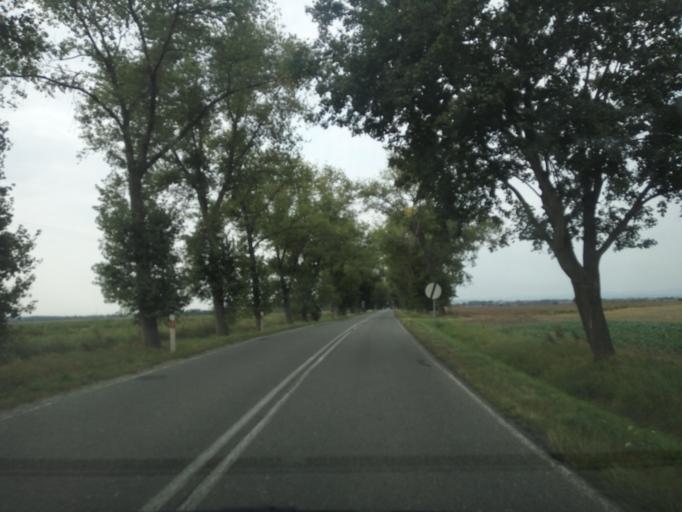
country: PL
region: Lower Silesian Voivodeship
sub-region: Powiat strzelinski
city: Strzelin
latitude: 50.8599
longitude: 17.0658
